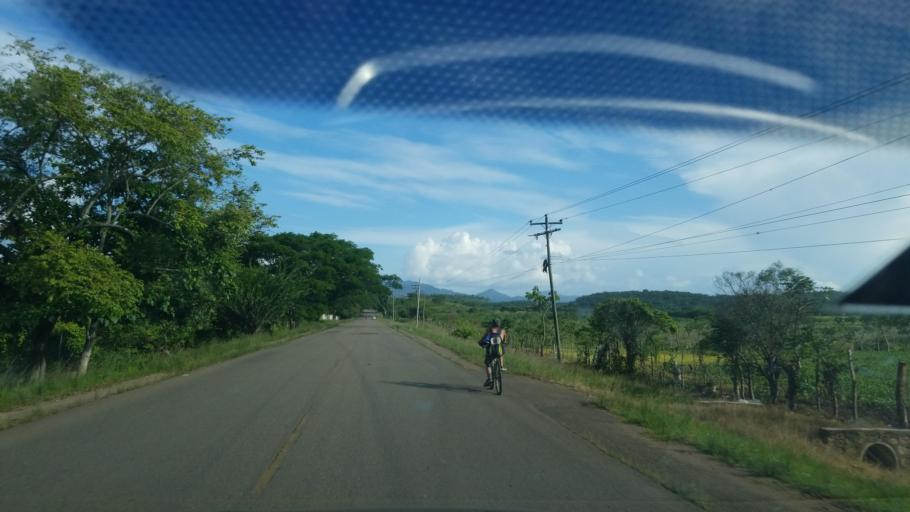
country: HN
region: El Paraiso
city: Arauli
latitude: 13.9341
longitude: -86.5584
